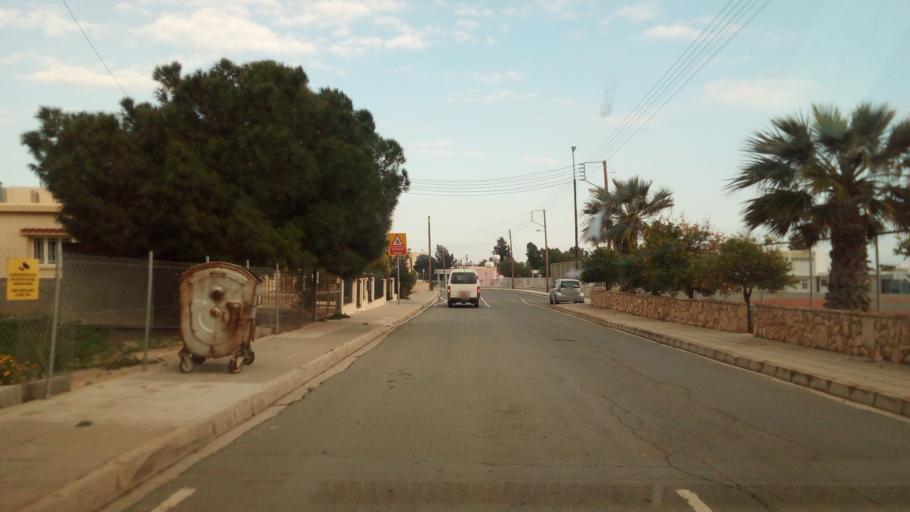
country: CY
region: Larnaka
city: Xylotymbou
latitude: 35.0128
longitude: 33.7352
